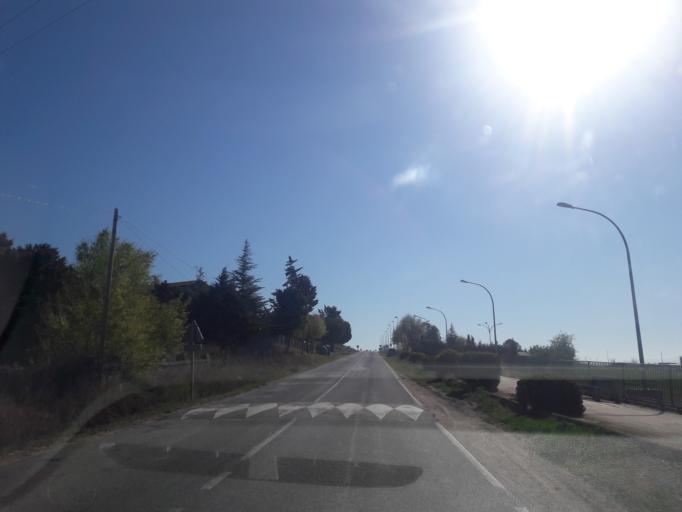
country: ES
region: Castille and Leon
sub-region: Provincia de Salamanca
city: Macotera
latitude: 40.8336
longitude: -5.2813
